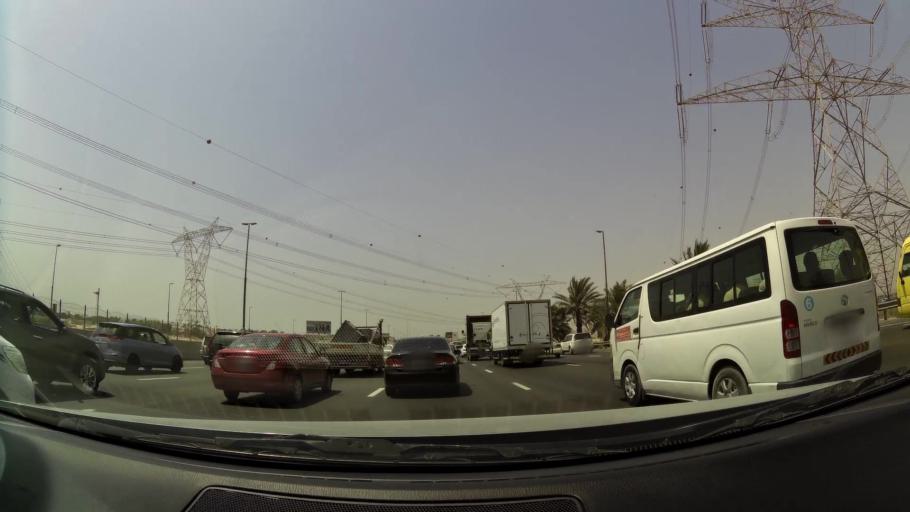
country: AE
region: Ash Shariqah
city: Sharjah
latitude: 25.2215
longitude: 55.4053
